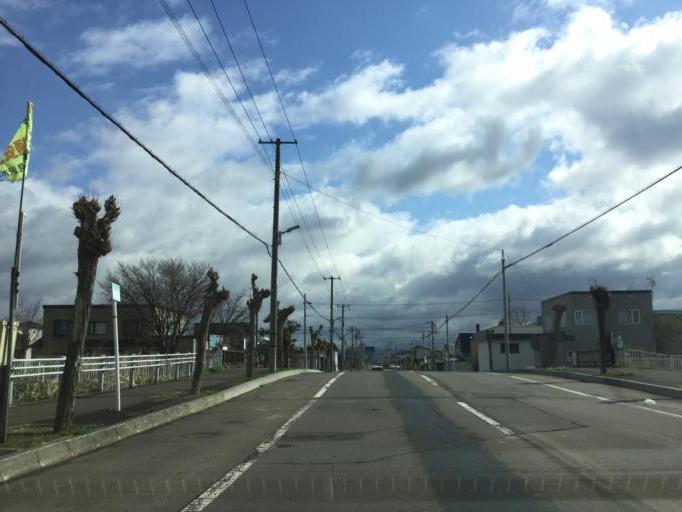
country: JP
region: Hokkaido
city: Iwamizawa
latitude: 43.2035
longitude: 141.7492
